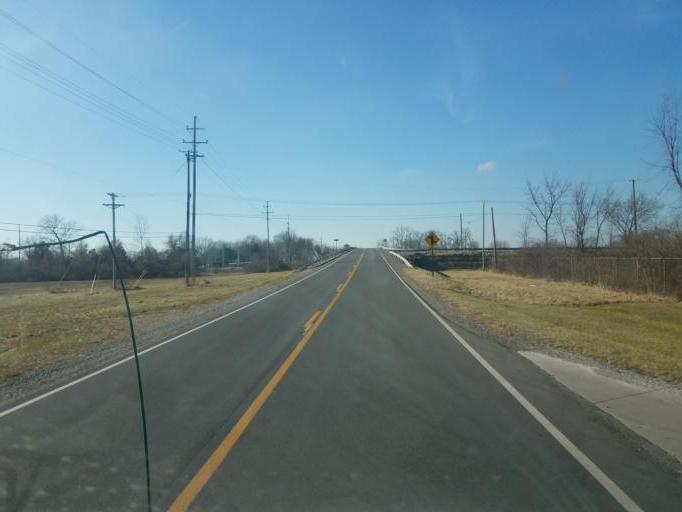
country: US
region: Ohio
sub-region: Marion County
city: Marion
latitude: 40.6299
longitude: -83.0937
